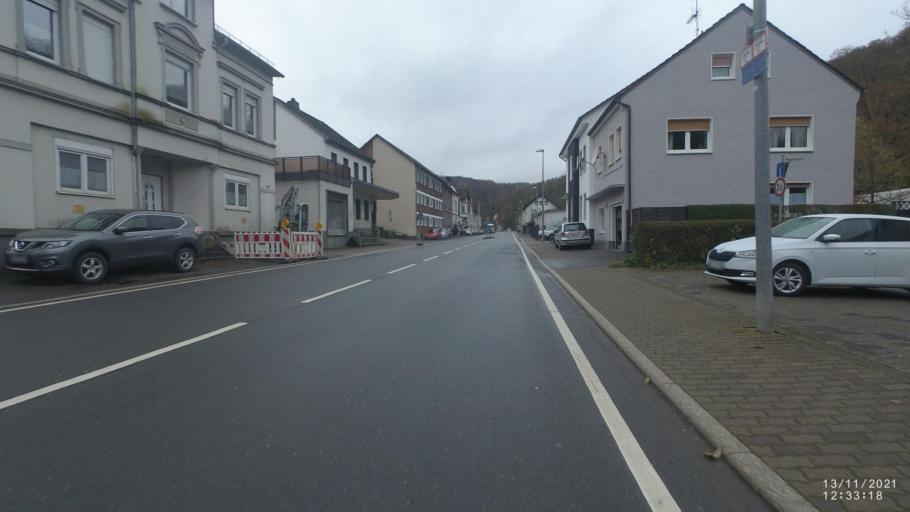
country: DE
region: North Rhine-Westphalia
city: Altena
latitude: 51.2556
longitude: 7.6628
